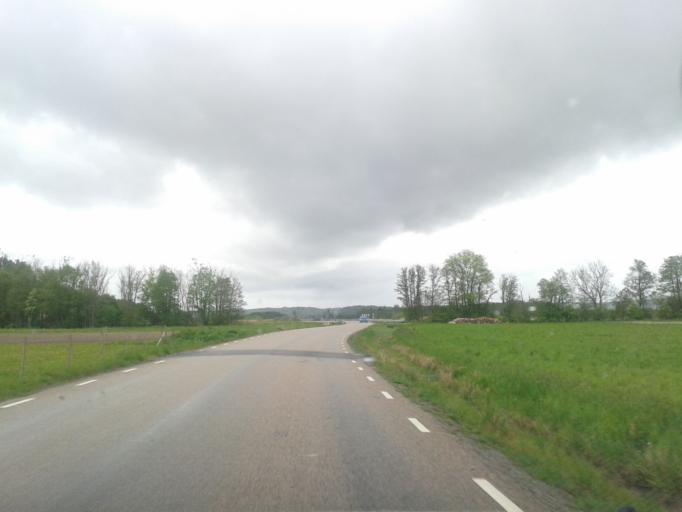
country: SE
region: Vaestra Goetaland
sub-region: Lilla Edets Kommun
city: Lodose
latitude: 58.0012
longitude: 12.1233
